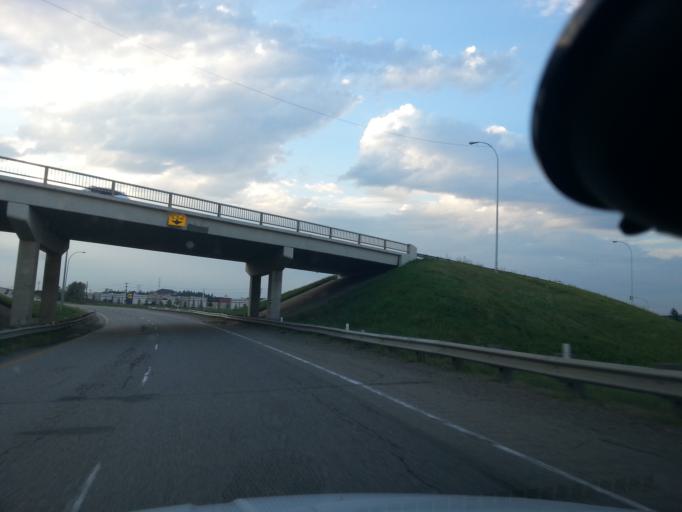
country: CA
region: Alberta
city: Red Deer
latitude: 52.2278
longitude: -113.8146
